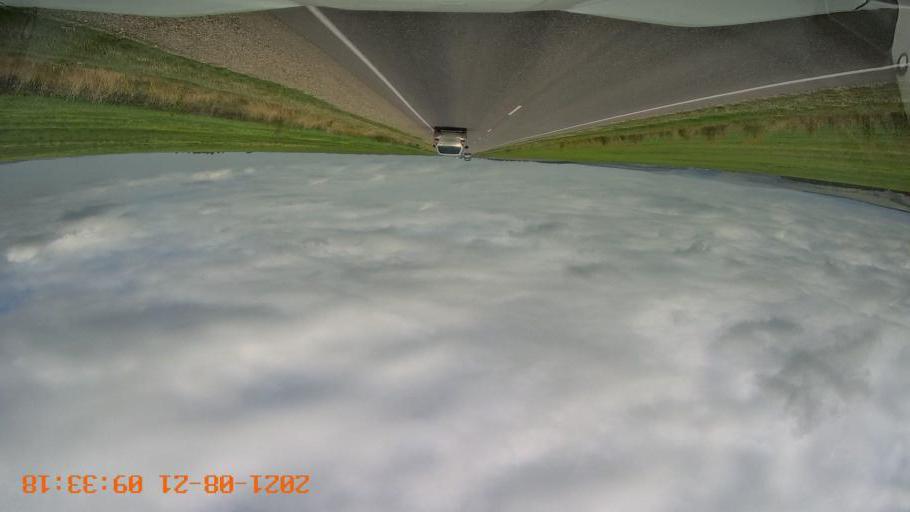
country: RU
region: Stavropol'skiy
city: Yutsa
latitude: 43.9928
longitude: 42.9930
